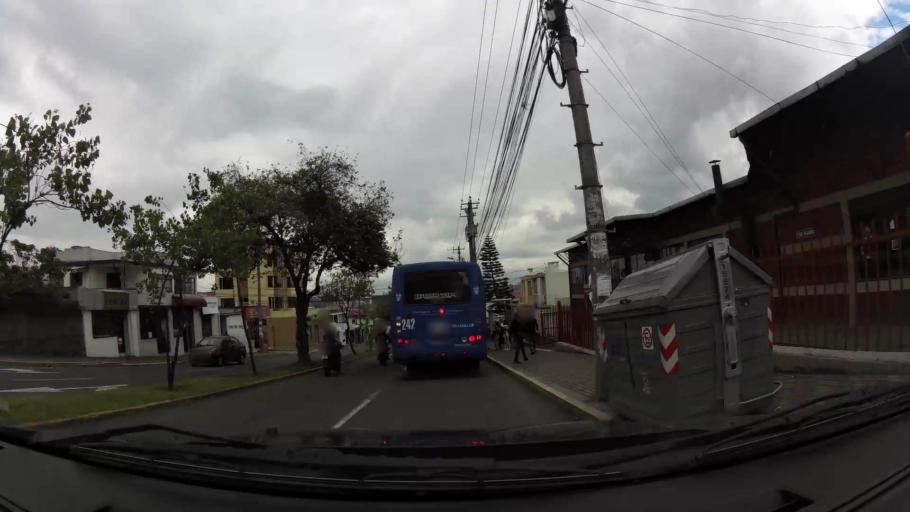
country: EC
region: Pichincha
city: Quito
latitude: -0.1953
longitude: -78.5076
